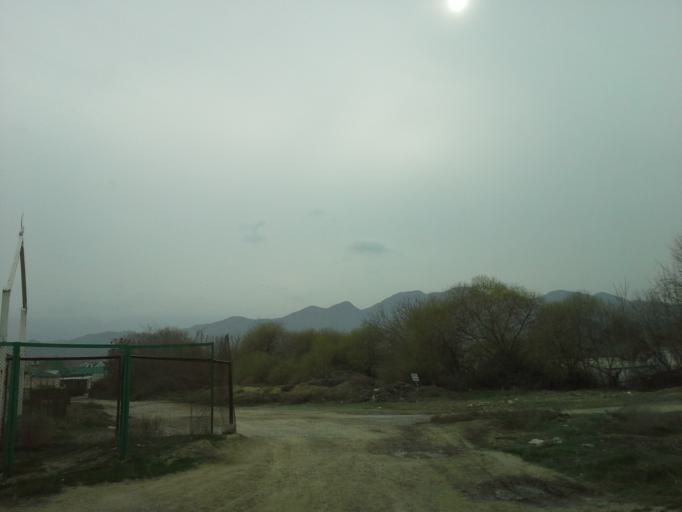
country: TM
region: Ahal
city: Abadan
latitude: 37.9698
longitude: 58.2225
